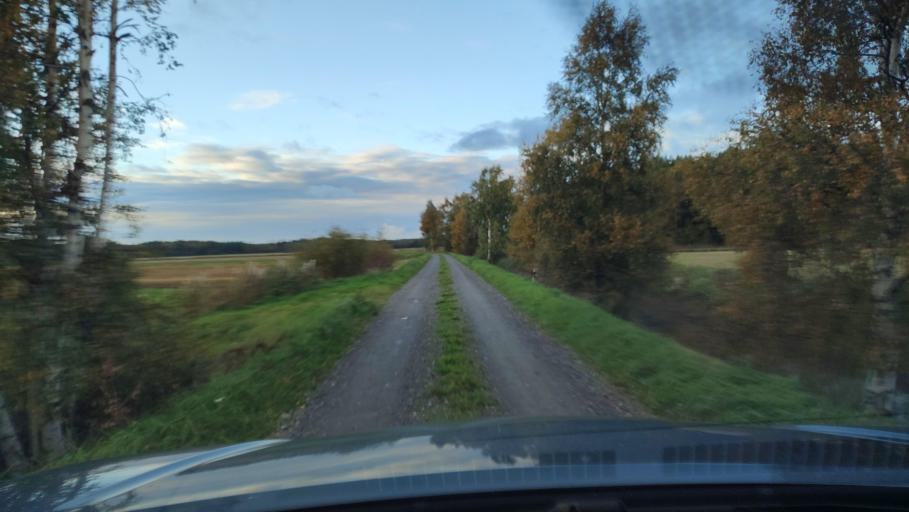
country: FI
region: Ostrobothnia
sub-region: Sydosterbotten
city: Kristinestad
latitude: 62.2435
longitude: 21.4530
